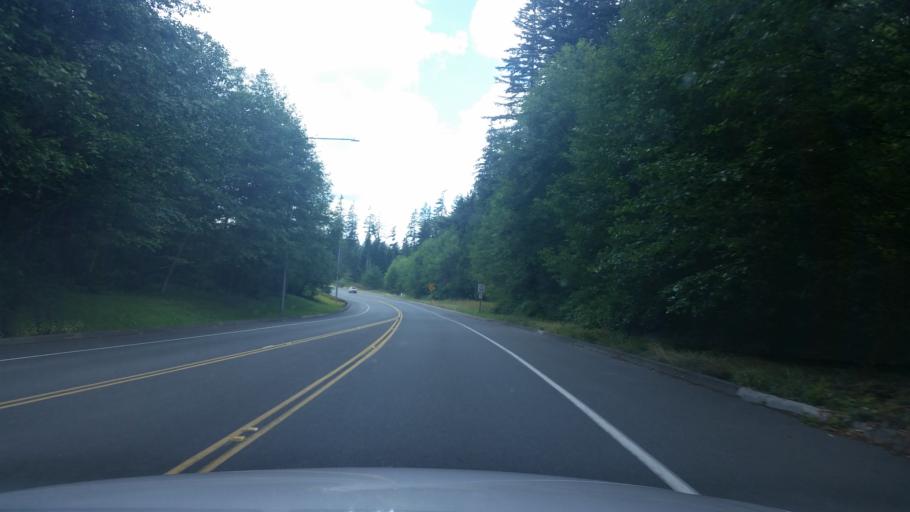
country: US
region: Washington
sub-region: King County
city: Union Hill-Novelty Hill
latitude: 47.7180
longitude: -122.0291
